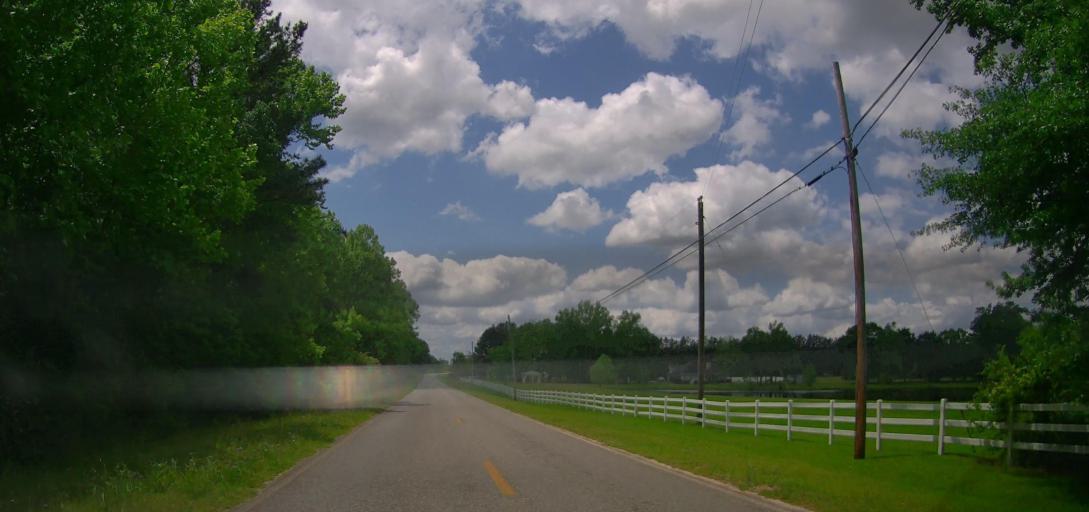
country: US
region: Georgia
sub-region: Laurens County
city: Dublin
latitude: 32.6059
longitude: -82.9465
